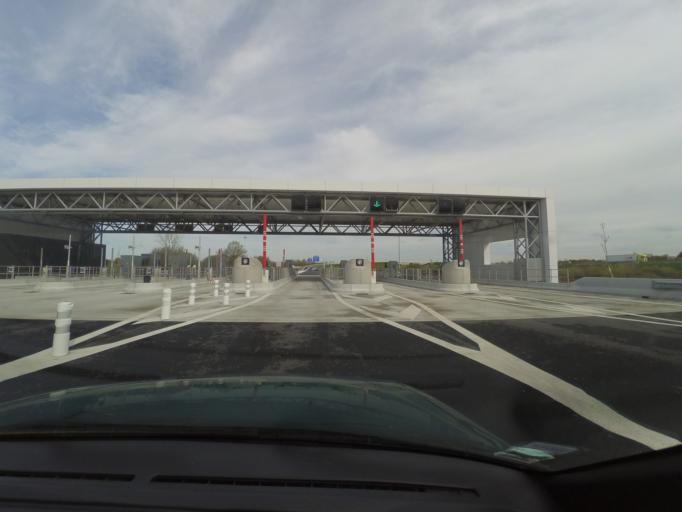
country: FR
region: Pays de la Loire
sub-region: Departement de la Loire-Atlantique
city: Aigrefeuille-sur-Maine
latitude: 47.0690
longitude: -1.4372
